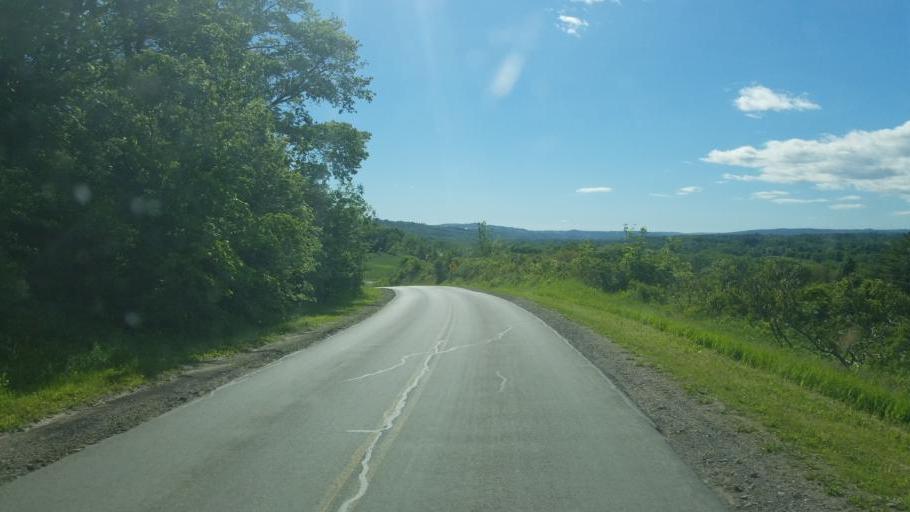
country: US
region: New York
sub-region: Montgomery County
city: Saint Johnsville
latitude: 42.9904
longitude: -74.6803
